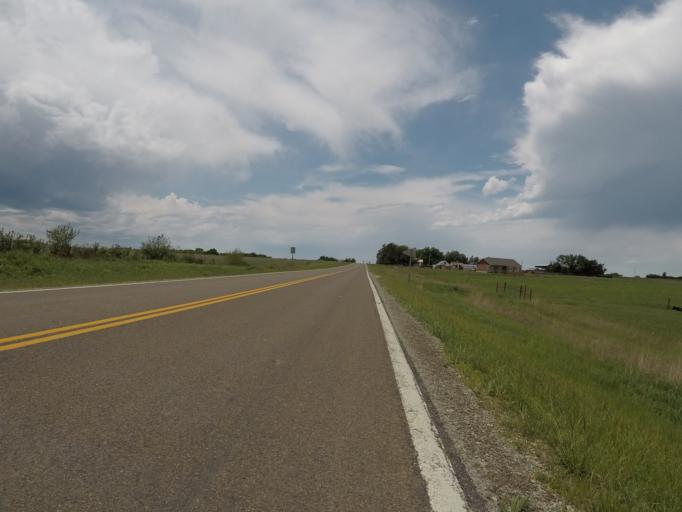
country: US
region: Kansas
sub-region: Wabaunsee County
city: Alma
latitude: 38.8550
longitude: -96.4064
